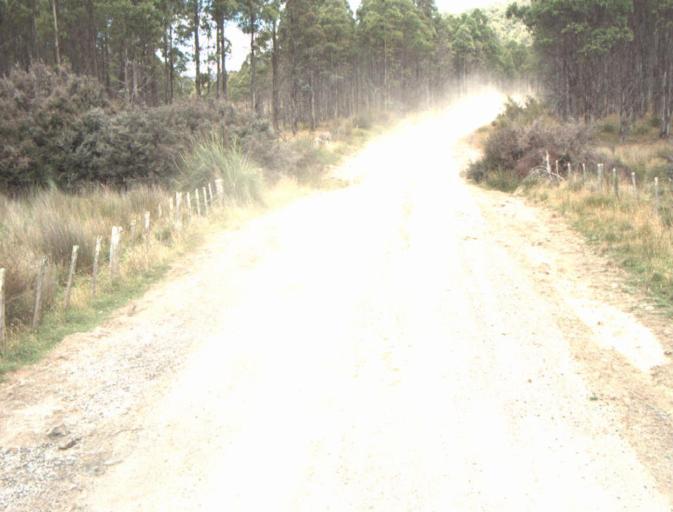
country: AU
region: Tasmania
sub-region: Dorset
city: Scottsdale
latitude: -41.4097
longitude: 147.5291
